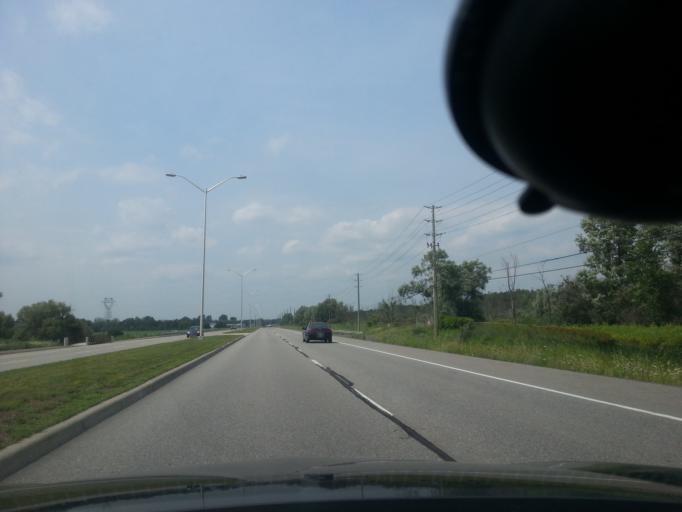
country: CA
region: Ontario
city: Ottawa
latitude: 45.3074
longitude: -75.6822
